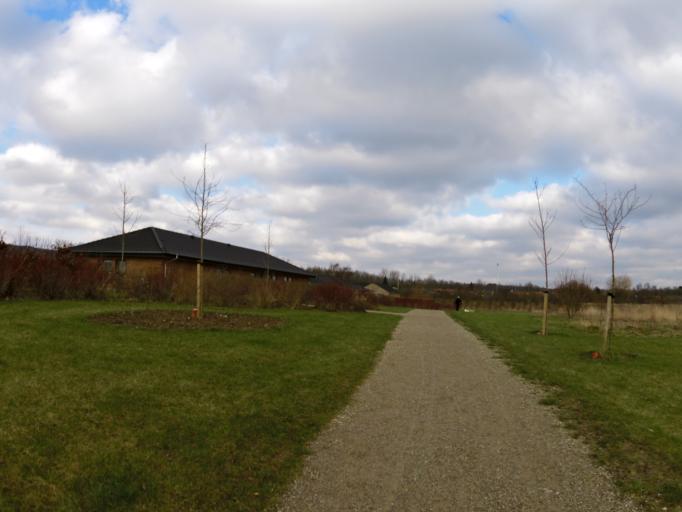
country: DK
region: Central Jutland
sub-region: Arhus Kommune
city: Tranbjerg
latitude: 56.0825
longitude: 10.1242
